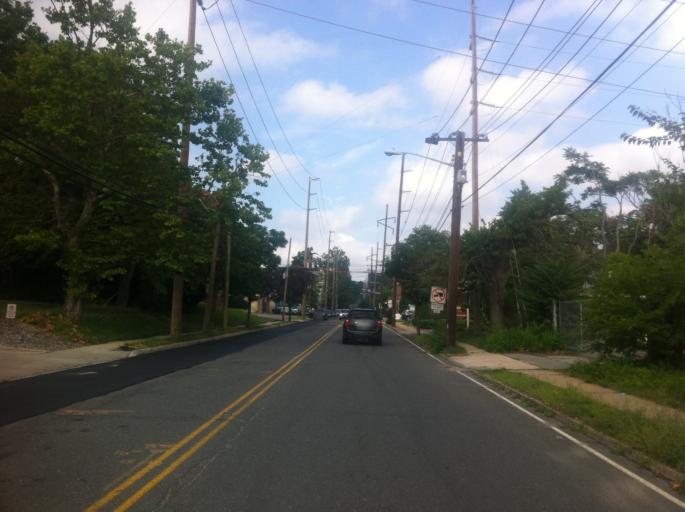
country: US
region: New York
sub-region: Nassau County
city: Sea Cliff
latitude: 40.8373
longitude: -73.6518
